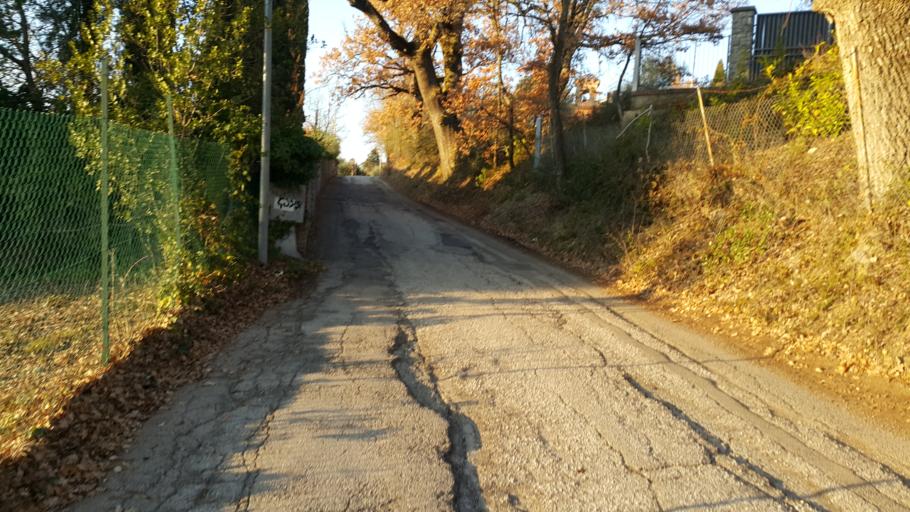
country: IT
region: Umbria
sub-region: Provincia di Perugia
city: Perugia
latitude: 43.0882
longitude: 12.3778
